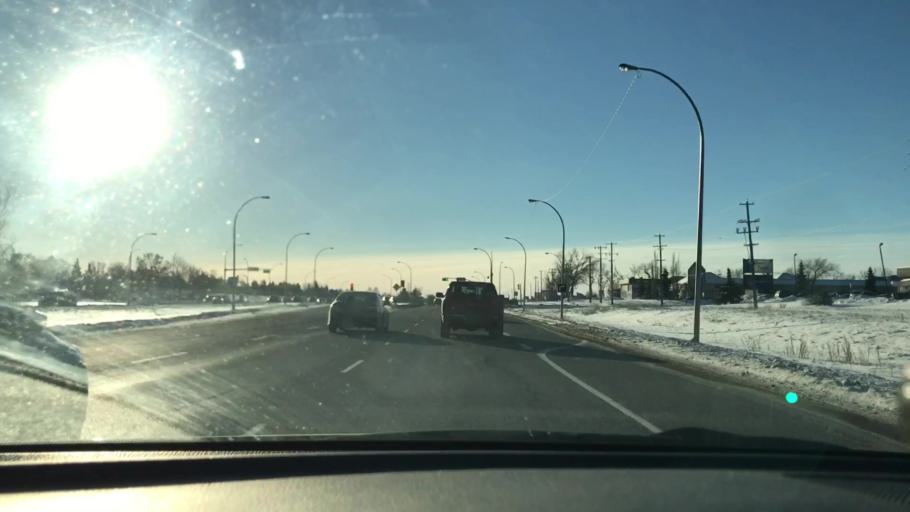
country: CA
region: Alberta
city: Edmonton
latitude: 53.4756
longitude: -113.4672
